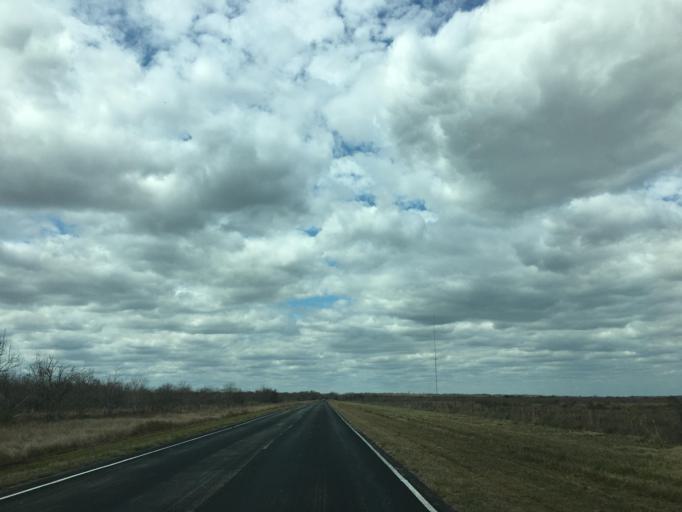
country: US
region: Texas
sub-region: Brazoria County
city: Oyster Creek
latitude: 29.0654
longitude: -95.3077
